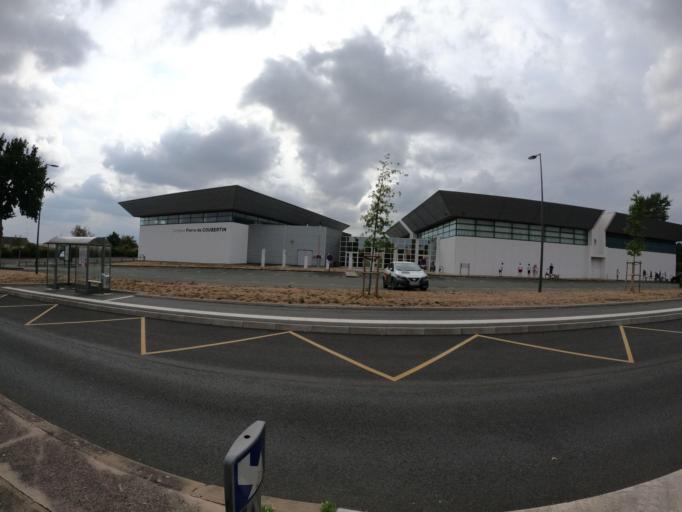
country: FR
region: Pays de la Loire
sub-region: Departement de Maine-et-Loire
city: La Seguiniere
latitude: 47.0667
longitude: -0.9367
